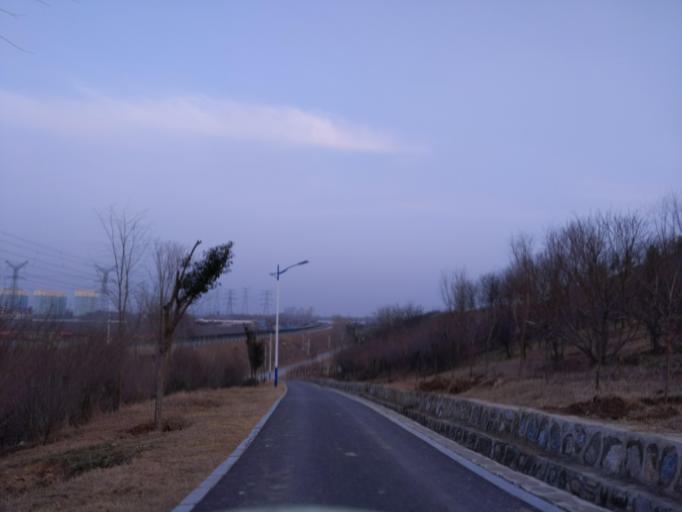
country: CN
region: Henan Sheng
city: Zhongyuanlu
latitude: 35.8158
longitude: 115.0587
